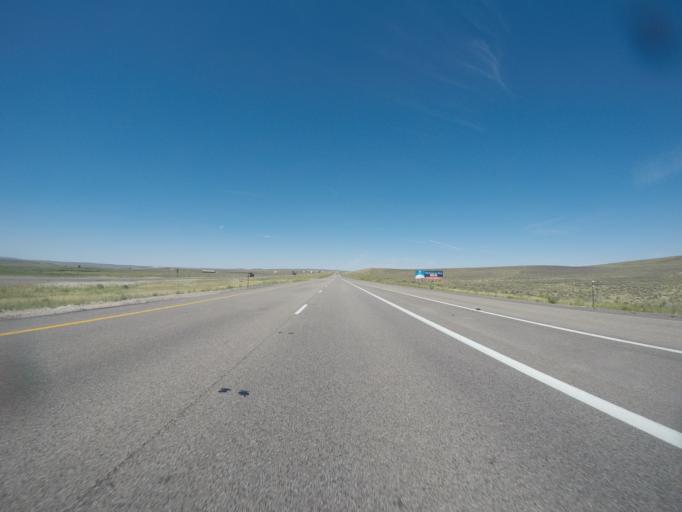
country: US
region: Wyoming
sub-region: Carbon County
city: Saratoga
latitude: 41.7431
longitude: -106.7773
